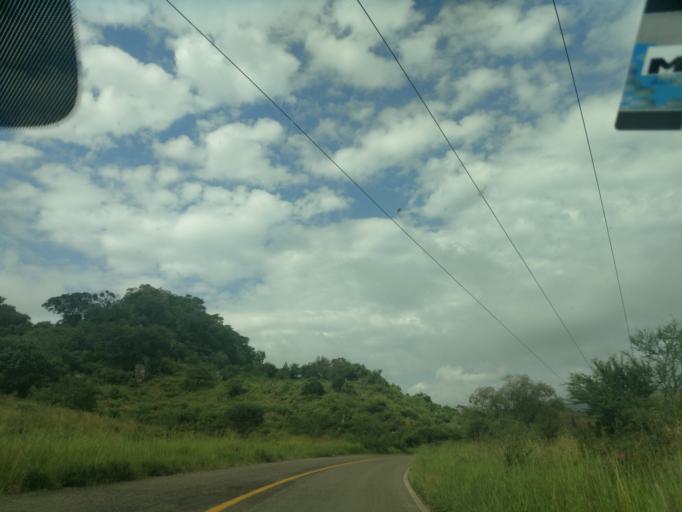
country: MX
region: Jalisco
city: El Salto
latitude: 20.4168
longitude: -104.5015
